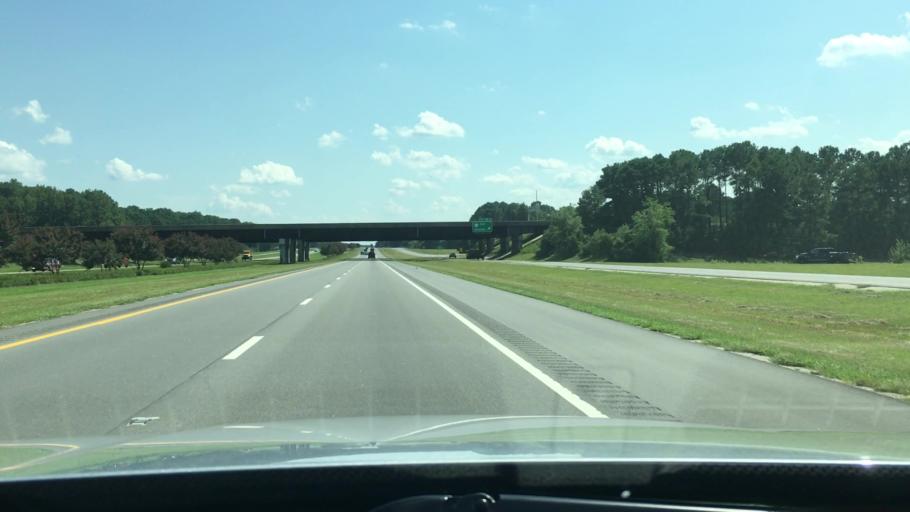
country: US
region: North Carolina
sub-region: Cumberland County
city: Vander
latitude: 35.0448
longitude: -78.8030
